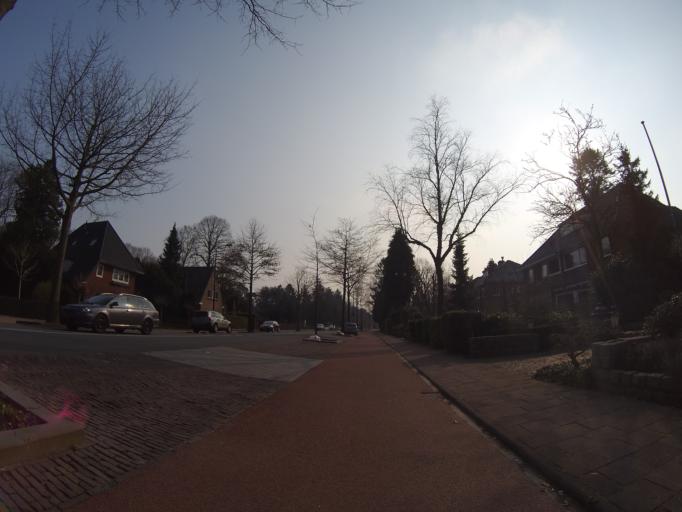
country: NL
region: Utrecht
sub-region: Gemeente Soest
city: Soest
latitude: 52.1611
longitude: 5.3082
